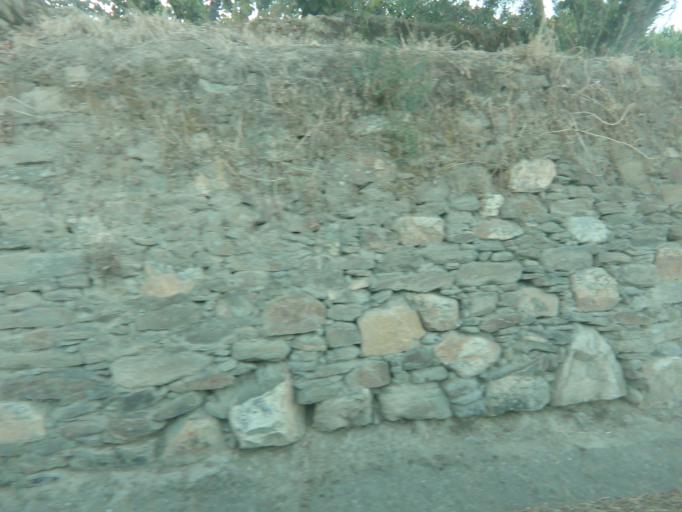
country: PT
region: Vila Real
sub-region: Peso da Regua
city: Godim
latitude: 41.1592
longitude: -7.8104
